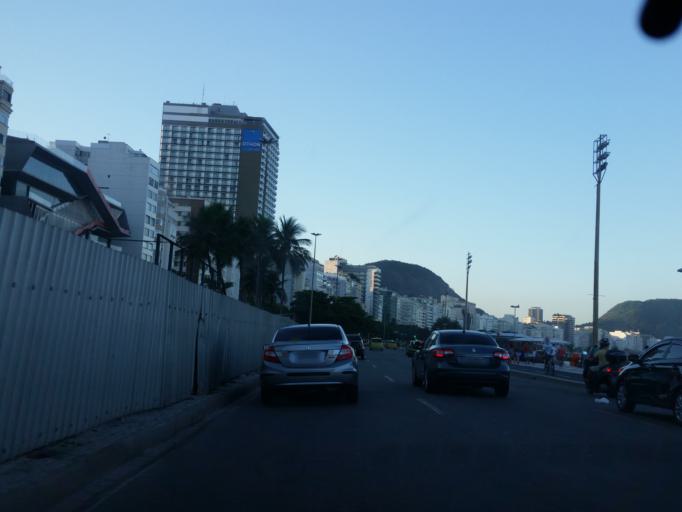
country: BR
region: Rio de Janeiro
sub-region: Rio De Janeiro
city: Rio de Janeiro
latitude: -22.9803
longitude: -43.1894
